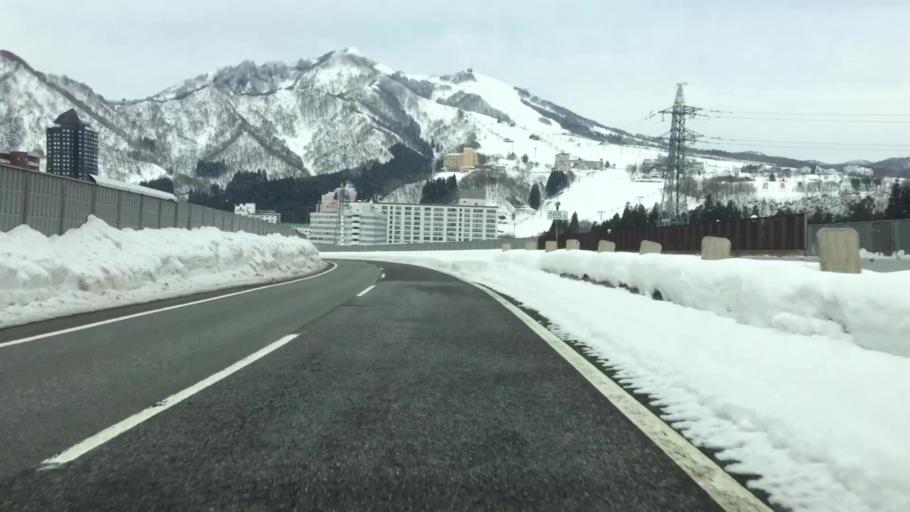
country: JP
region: Niigata
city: Shiozawa
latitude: 36.9244
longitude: 138.8414
